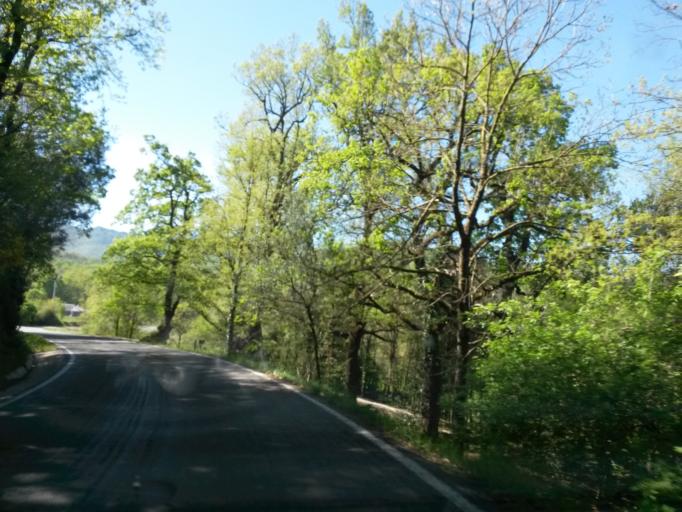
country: ES
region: Catalonia
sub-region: Provincia de Girona
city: Sant Cristofol de les Fonts
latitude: 42.1709
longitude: 2.5033
